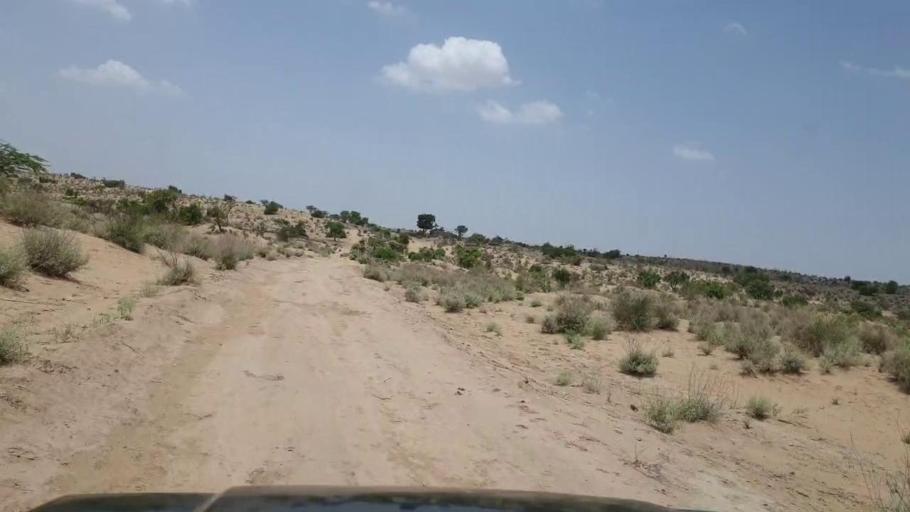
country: PK
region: Sindh
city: Umarkot
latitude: 25.1710
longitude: 69.8444
